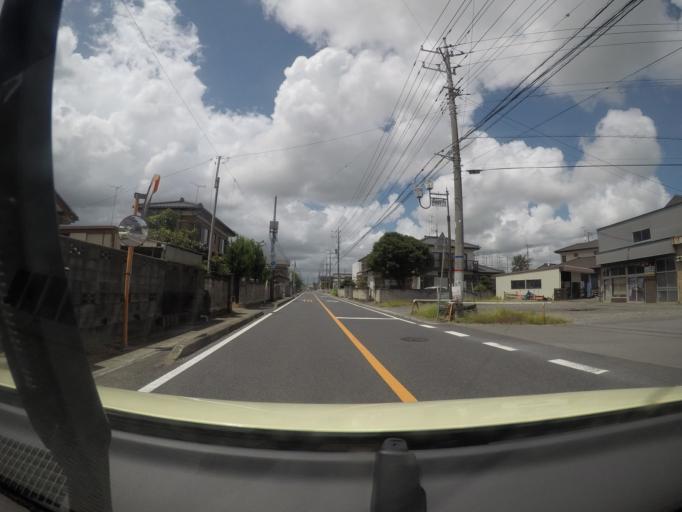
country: JP
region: Ibaraki
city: Mitsukaido
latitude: 36.0298
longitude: 139.9904
